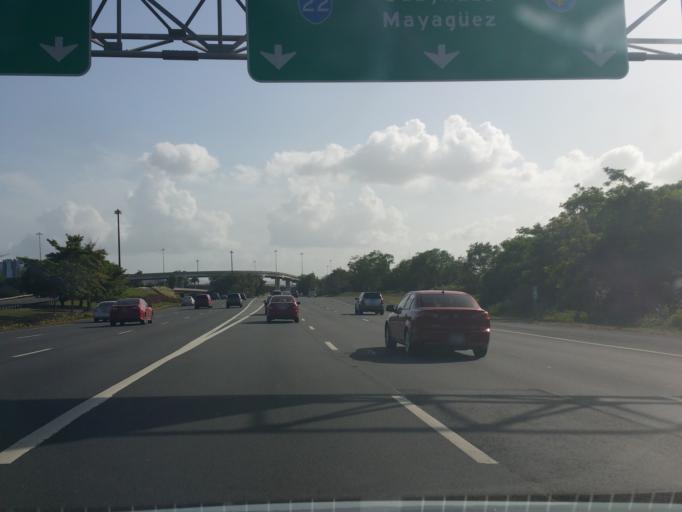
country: PR
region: Catano
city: Catano
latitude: 18.4327
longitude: -66.0743
